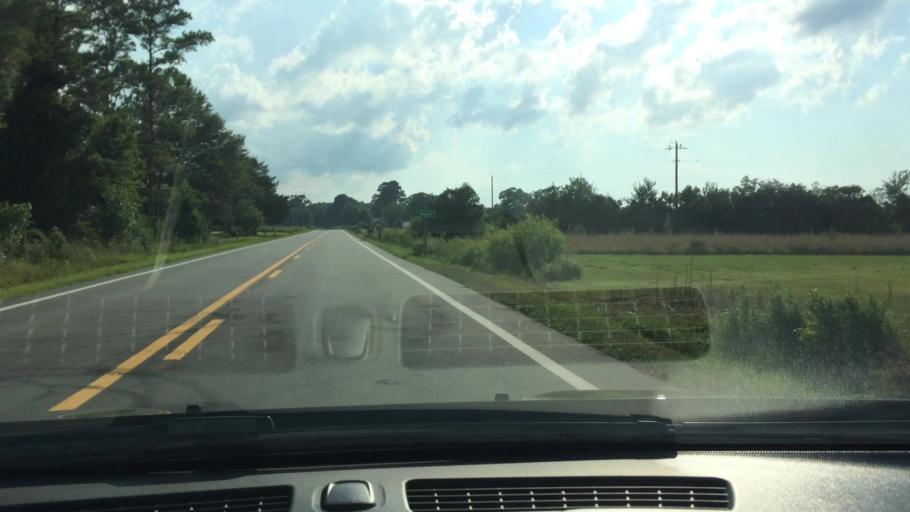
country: US
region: North Carolina
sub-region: Craven County
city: Vanceboro
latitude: 35.4383
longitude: -77.1552
